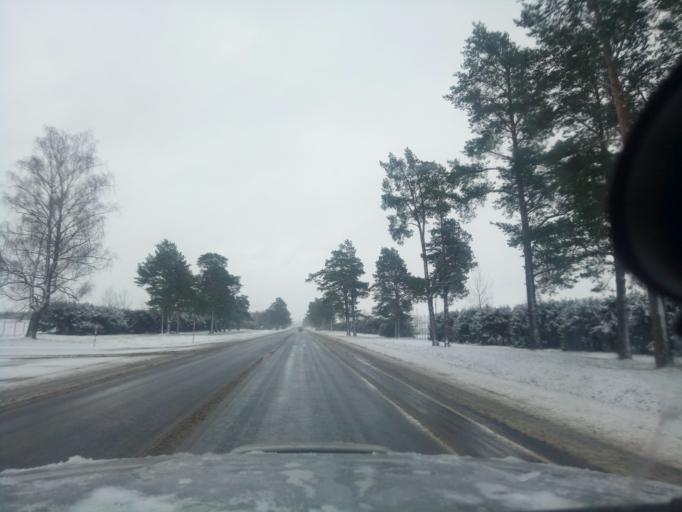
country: BY
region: Minsk
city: Nyasvizh
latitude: 53.2517
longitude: 26.6199
